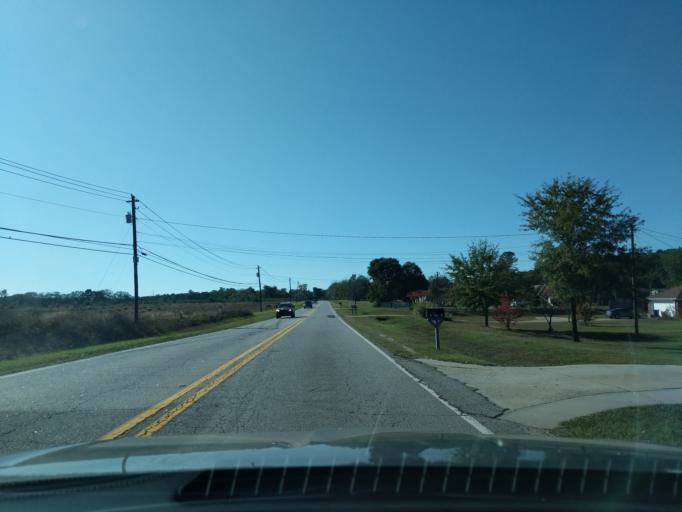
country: US
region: Georgia
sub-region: Columbia County
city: Grovetown
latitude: 33.4664
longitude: -82.1625
